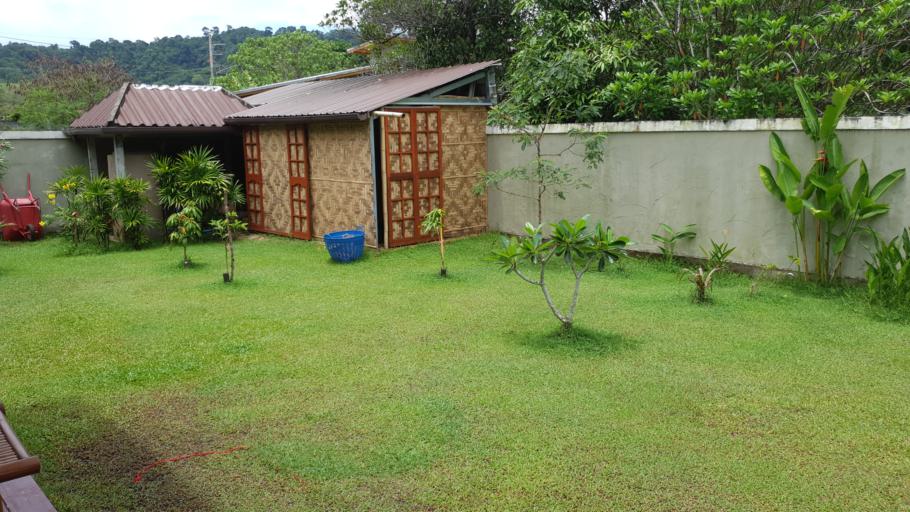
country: TH
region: Phuket
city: Thalang
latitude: 8.0199
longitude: 98.3468
